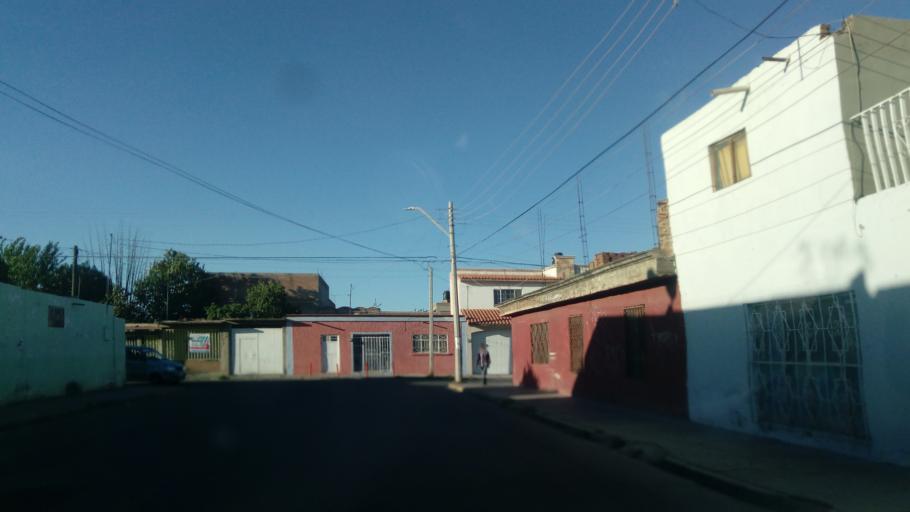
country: MX
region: Durango
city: Victoria de Durango
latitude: 24.0014
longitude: -104.6742
